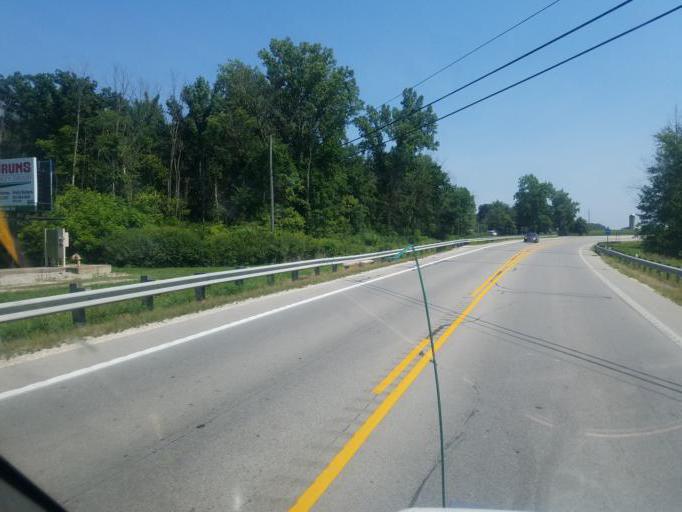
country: US
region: Ohio
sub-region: Mercer County
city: Celina
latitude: 40.5006
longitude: -84.5725
